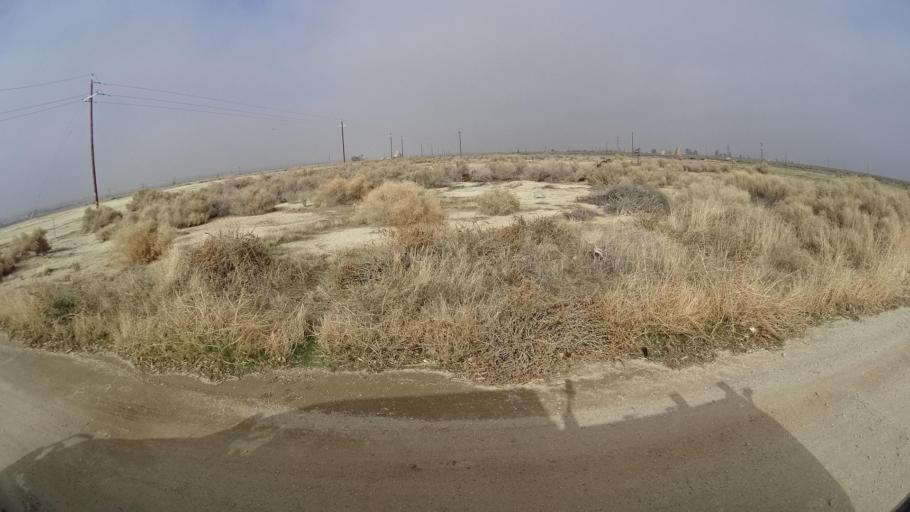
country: US
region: California
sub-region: Kern County
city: Maricopa
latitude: 35.0471
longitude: -119.3576
